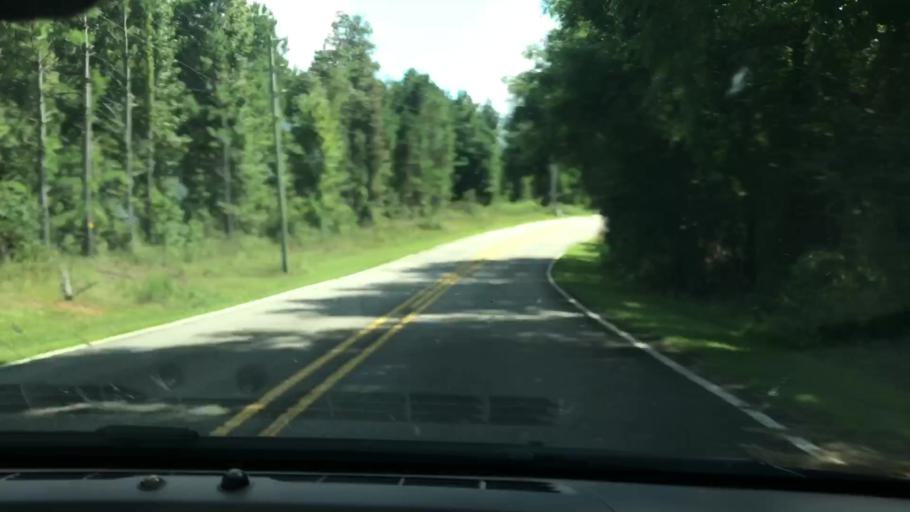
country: US
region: Georgia
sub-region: Troup County
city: La Grange
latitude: 33.1172
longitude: -85.1244
